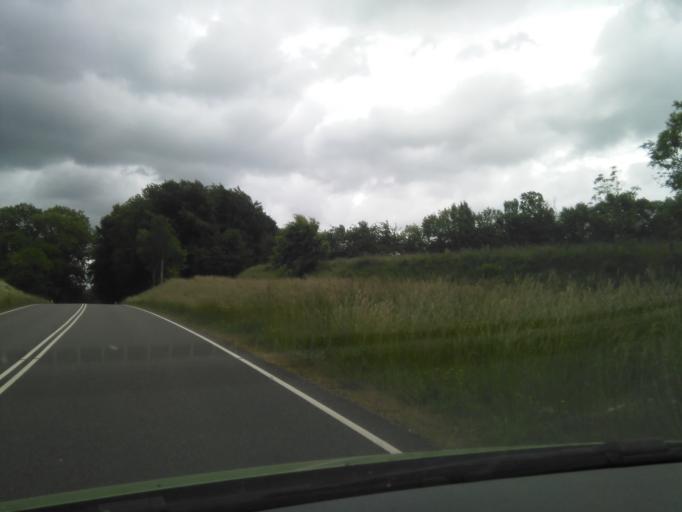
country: DK
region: Capital Region
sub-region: Bornholm Kommune
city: Akirkeby
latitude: 55.2297
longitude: 14.8789
